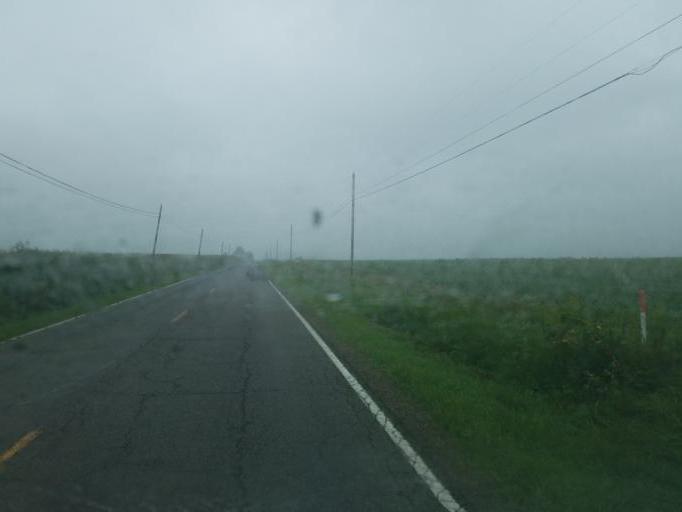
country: US
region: Ohio
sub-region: Licking County
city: Johnstown
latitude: 40.1892
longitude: -82.6924
